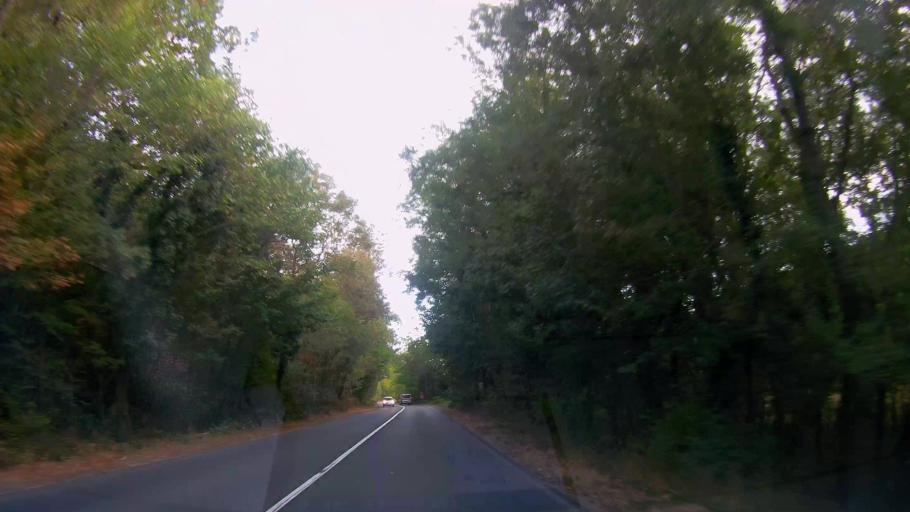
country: BG
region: Burgas
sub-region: Obshtina Primorsko
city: Primorsko
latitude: 42.3104
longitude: 27.7247
